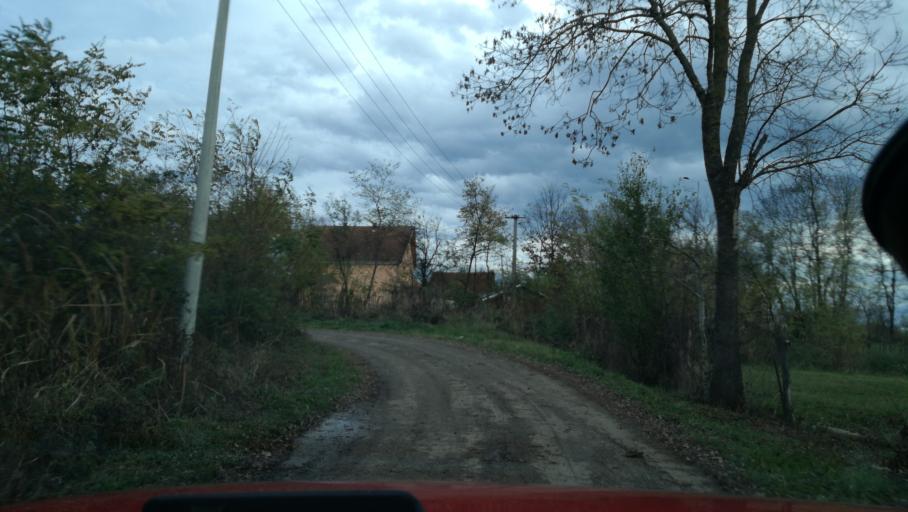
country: RS
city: Prislonica
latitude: 43.9060
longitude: 20.4317
